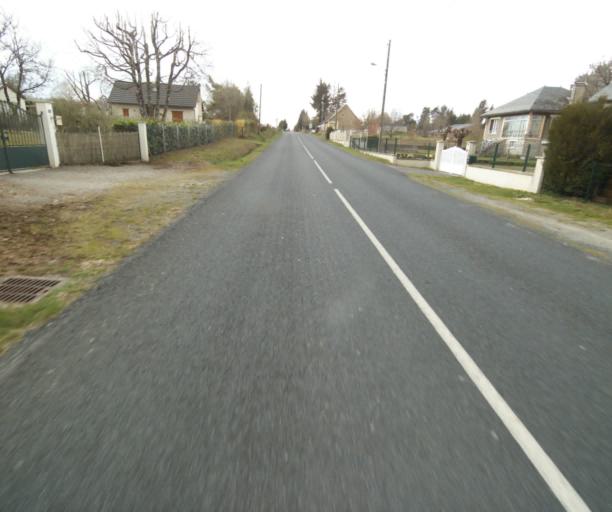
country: FR
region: Limousin
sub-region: Departement de la Correze
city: Correze
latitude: 45.2779
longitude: 1.9804
